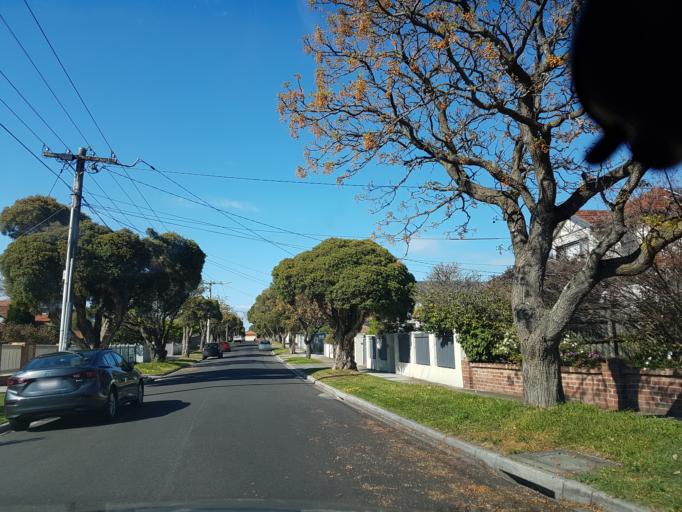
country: AU
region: Victoria
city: Ormond
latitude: -37.9082
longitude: 145.0319
